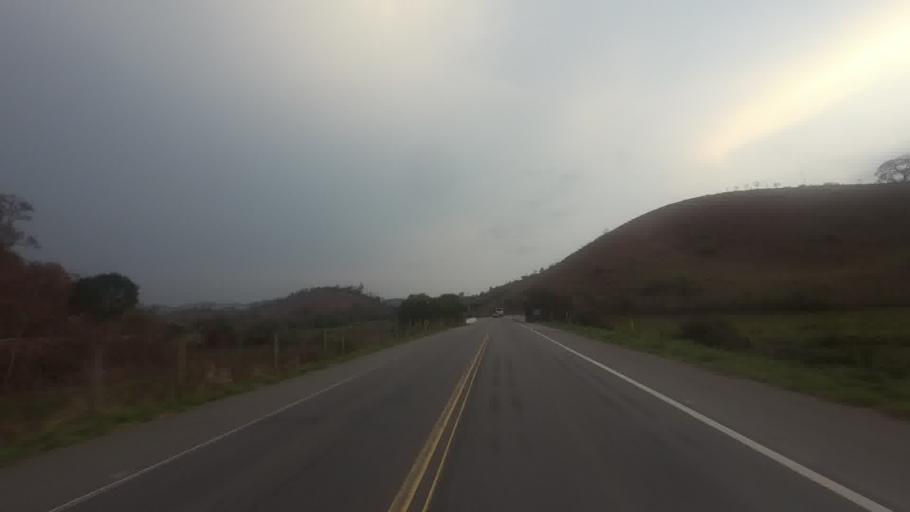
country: BR
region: Rio de Janeiro
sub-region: Carmo
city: Carmo
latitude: -21.8270
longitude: -42.6061
